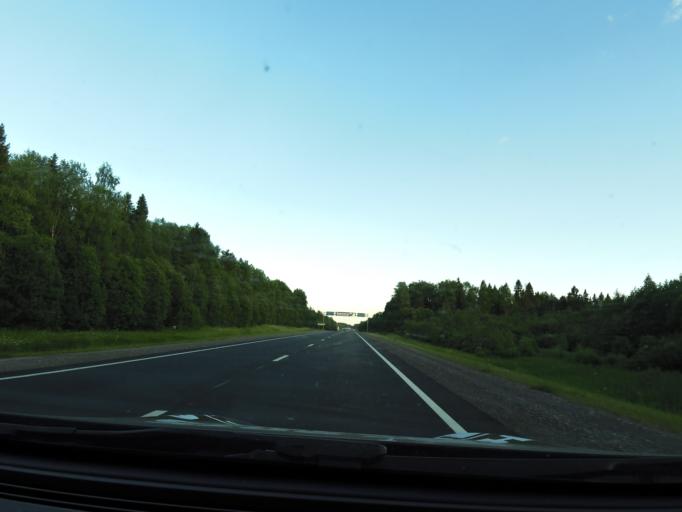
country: RU
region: Vologda
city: Gryazovets
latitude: 58.8967
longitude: 40.1856
